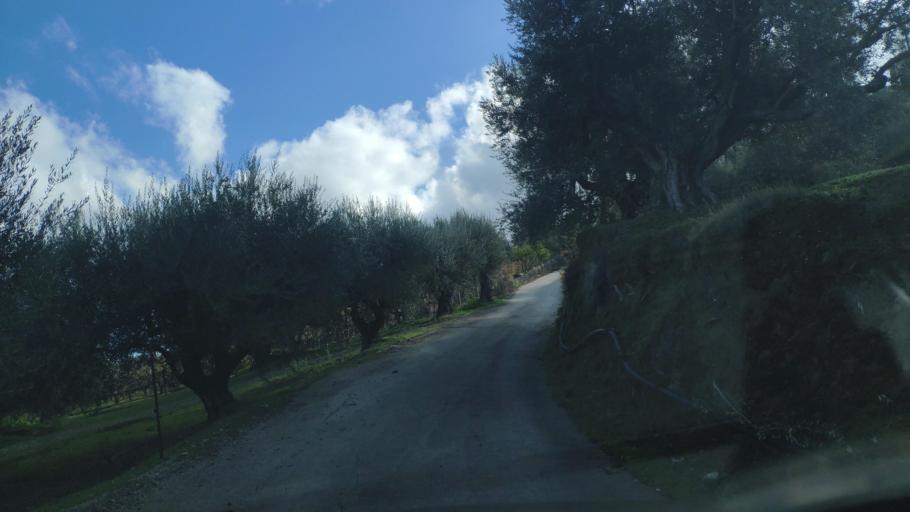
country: GR
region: West Greece
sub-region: Nomos Achaias
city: Aiyira
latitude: 38.1053
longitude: 22.4433
